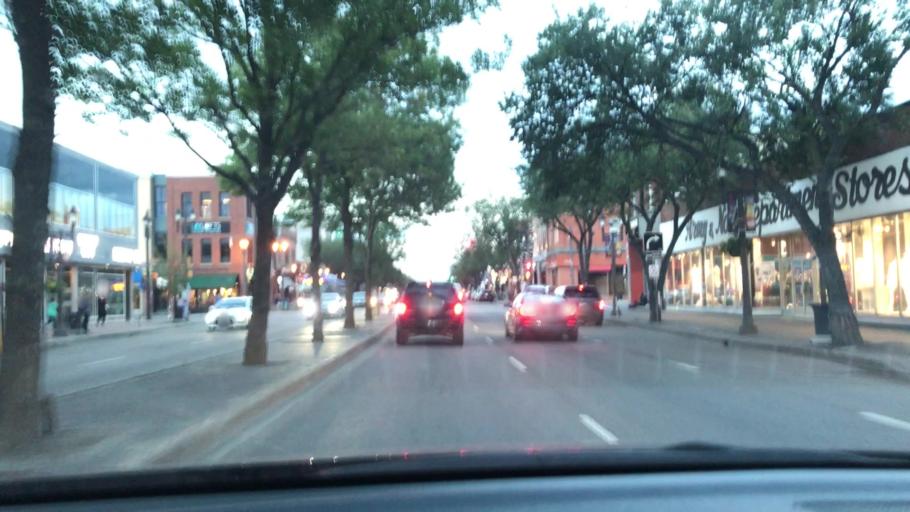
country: CA
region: Alberta
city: Edmonton
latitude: 53.5181
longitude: -113.4987
